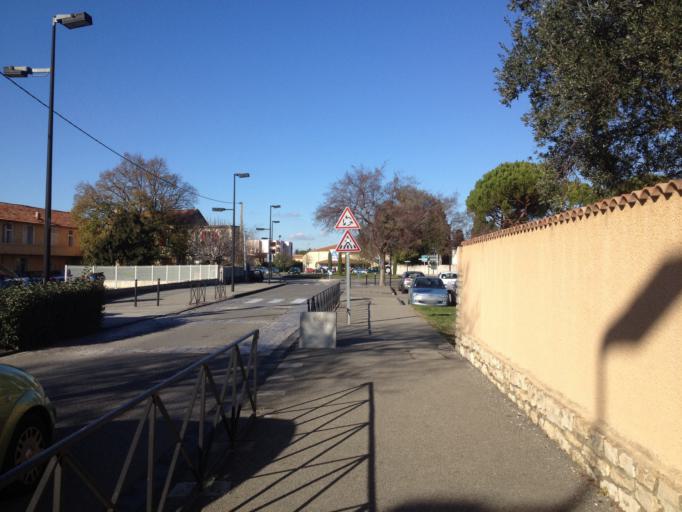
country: FR
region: Provence-Alpes-Cote d'Azur
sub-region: Departement du Vaucluse
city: Orange
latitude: 44.1435
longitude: 4.8015
